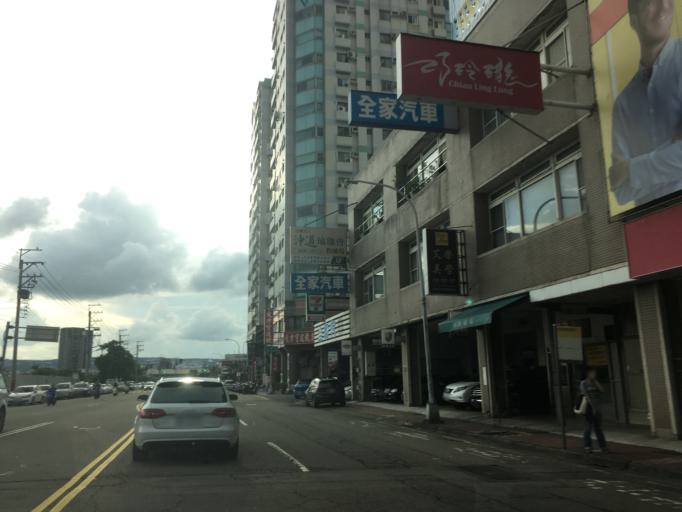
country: TW
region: Taiwan
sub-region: Taichung City
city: Taichung
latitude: 24.1357
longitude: 120.6367
